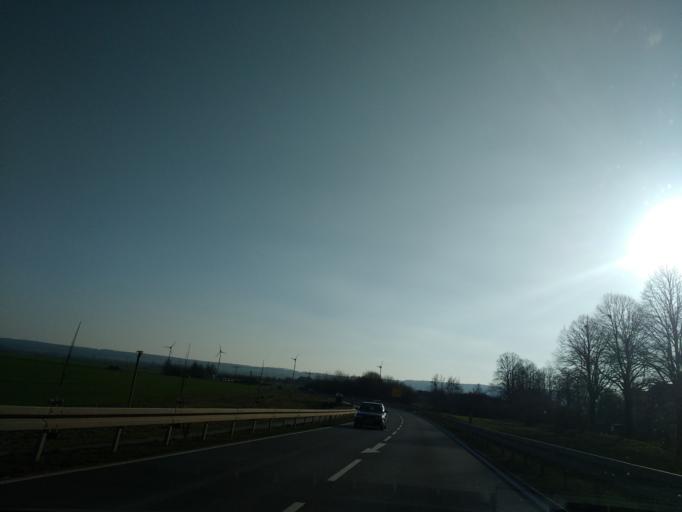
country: DE
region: Lower Saxony
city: Hessisch Oldendorf
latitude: 52.1564
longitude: 9.2486
